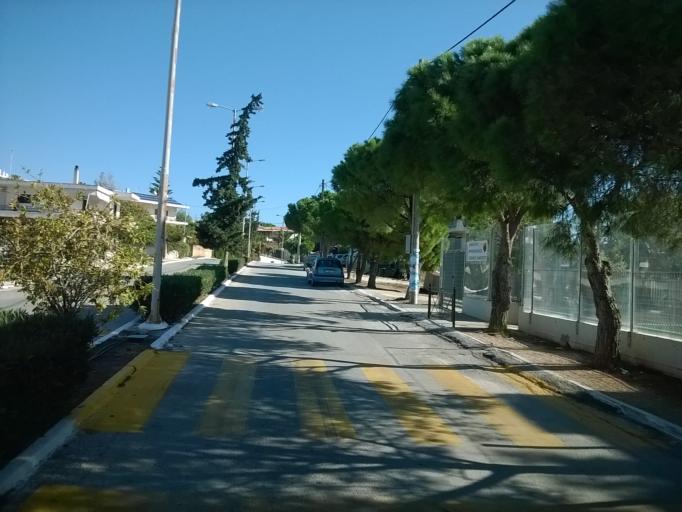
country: GR
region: Attica
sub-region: Nomarchia Anatolikis Attikis
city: Anavyssos
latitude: 37.7383
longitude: 23.9495
